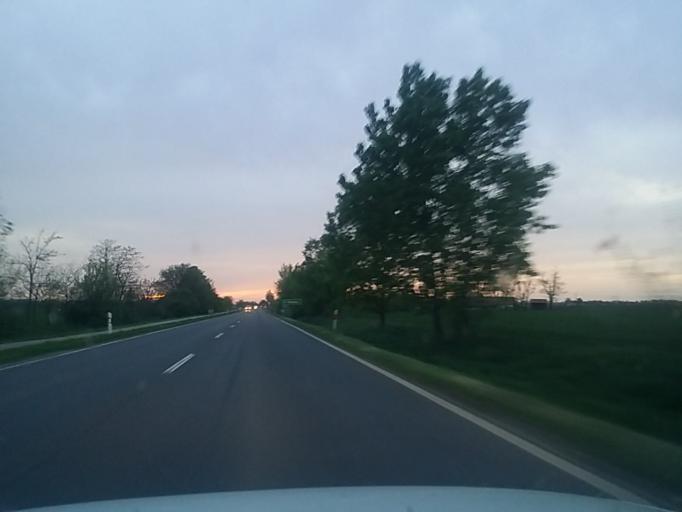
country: HU
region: Bekes
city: Kondoros
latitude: 46.7278
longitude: 20.9163
